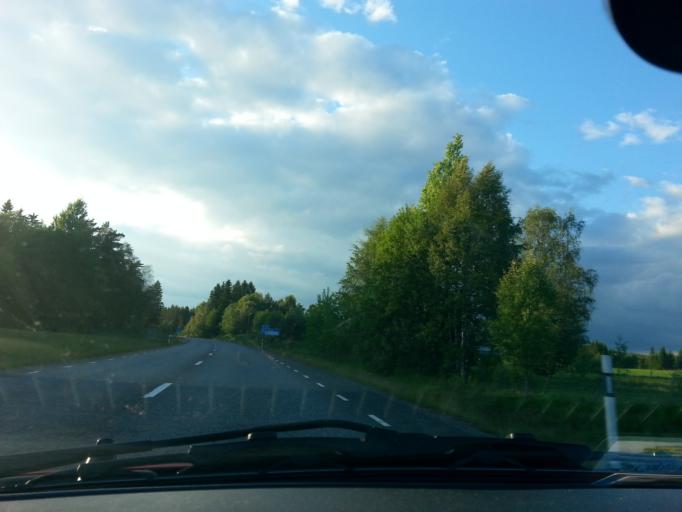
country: SE
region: Vaestra Goetaland
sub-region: Tranemo Kommun
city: Tranemo
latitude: 57.4309
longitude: 13.4468
